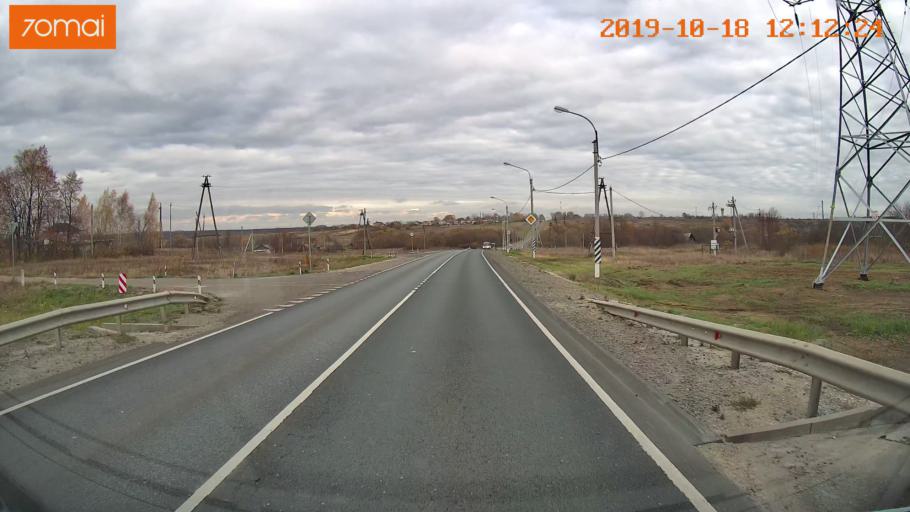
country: RU
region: Rjazan
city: Zakharovo
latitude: 54.4113
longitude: 39.3578
